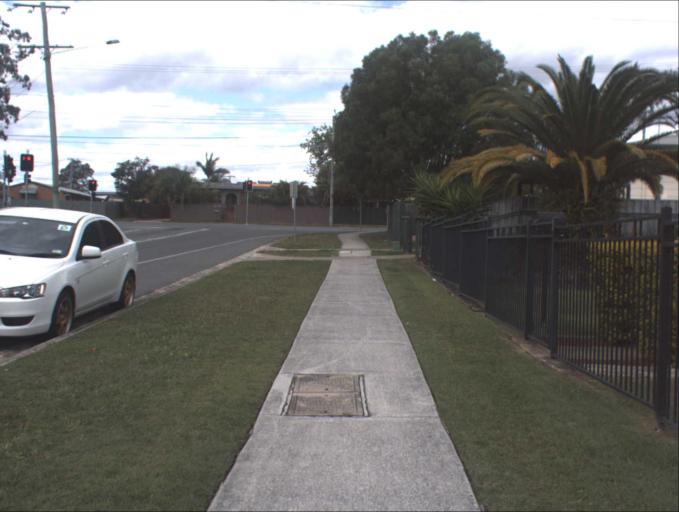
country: AU
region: Queensland
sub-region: Logan
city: Waterford West
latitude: -27.6811
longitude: 153.0999
